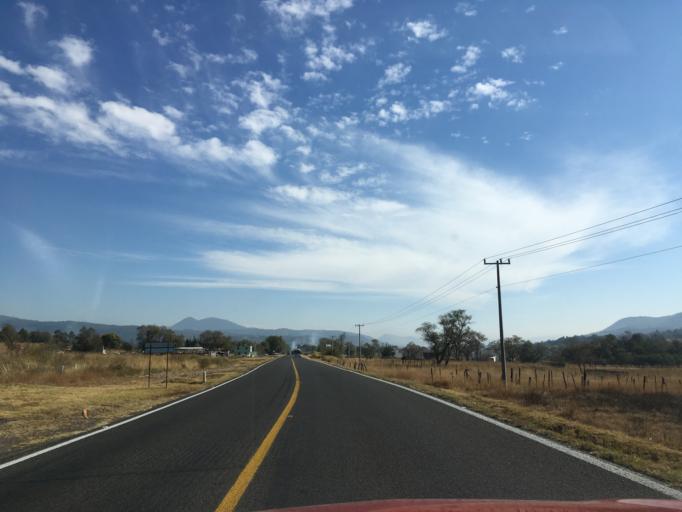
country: MX
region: Michoacan
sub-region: Hidalgo
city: San Lucas Huarirapeo (La Mesa de San Lucas)
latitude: 19.6815
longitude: -100.6403
